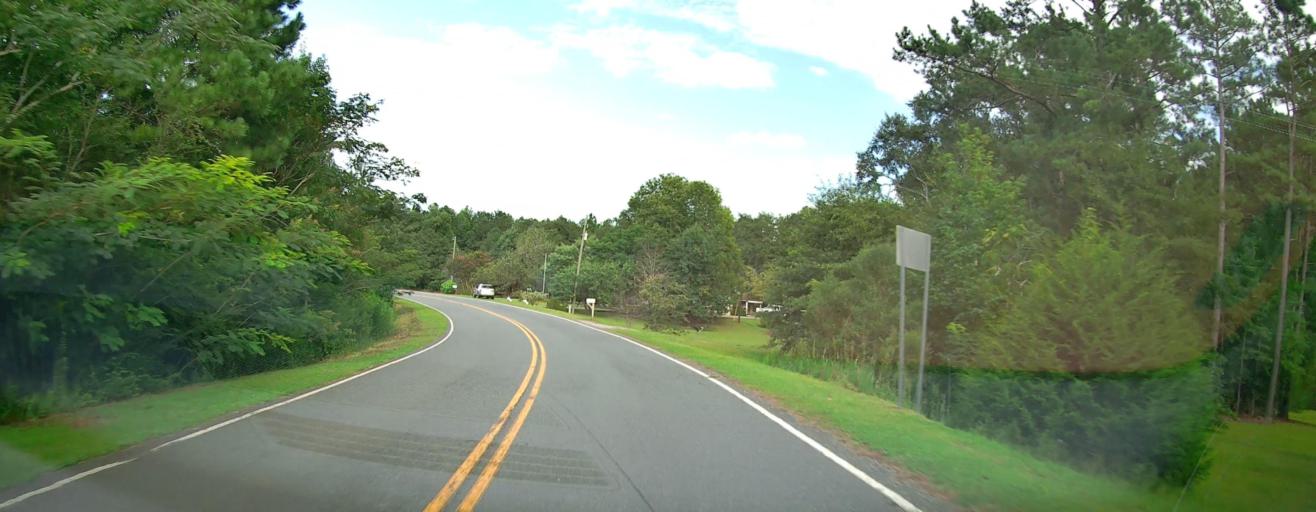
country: US
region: Georgia
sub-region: Meriwether County
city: Manchester
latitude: 32.9648
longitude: -84.6010
